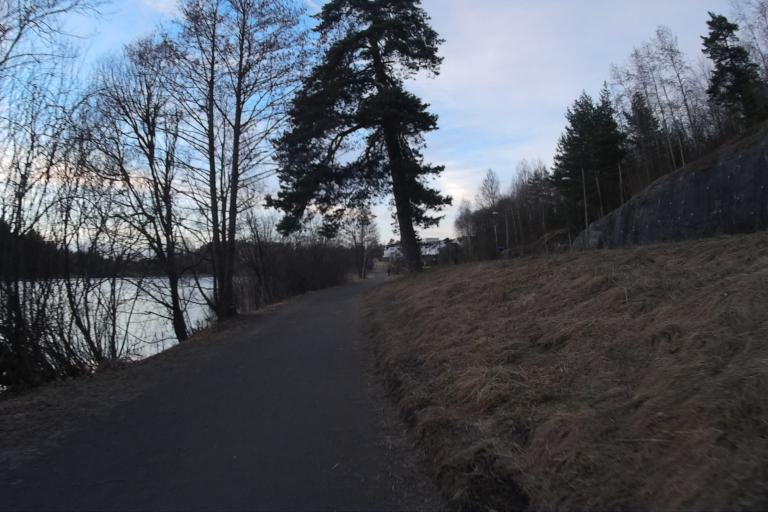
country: NO
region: Oslo
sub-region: Oslo
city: Oslo
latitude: 59.8945
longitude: 10.8325
